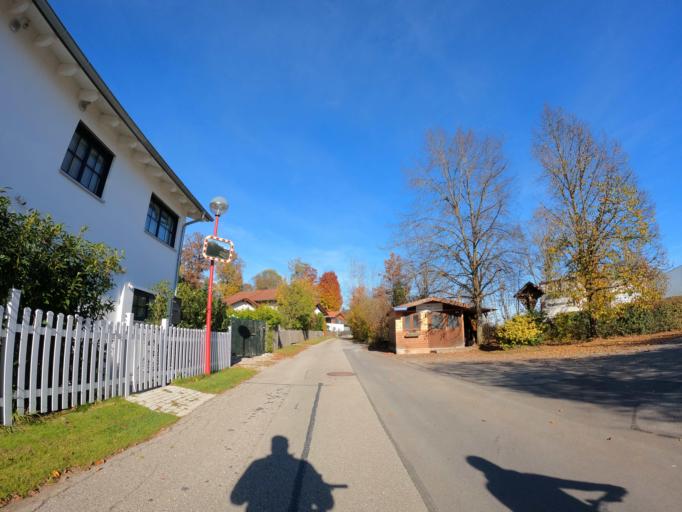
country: DE
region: Bavaria
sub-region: Upper Bavaria
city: Oberhaching
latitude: 48.0343
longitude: 11.5992
